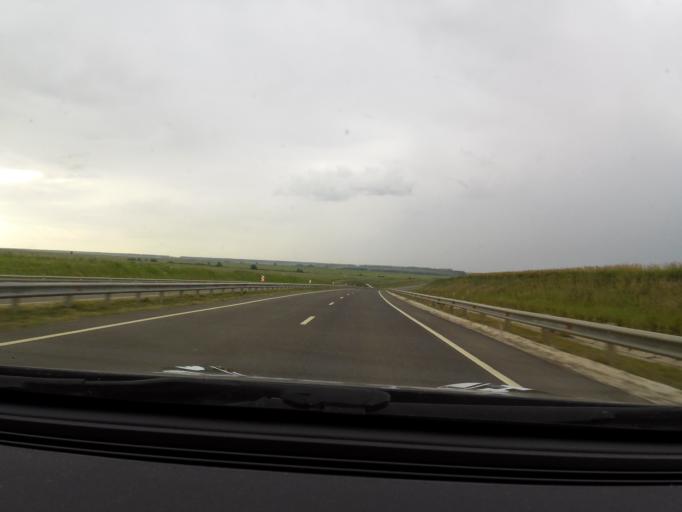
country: RU
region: Bashkortostan
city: Kushnarenkovo
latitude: 55.0652
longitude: 55.3090
